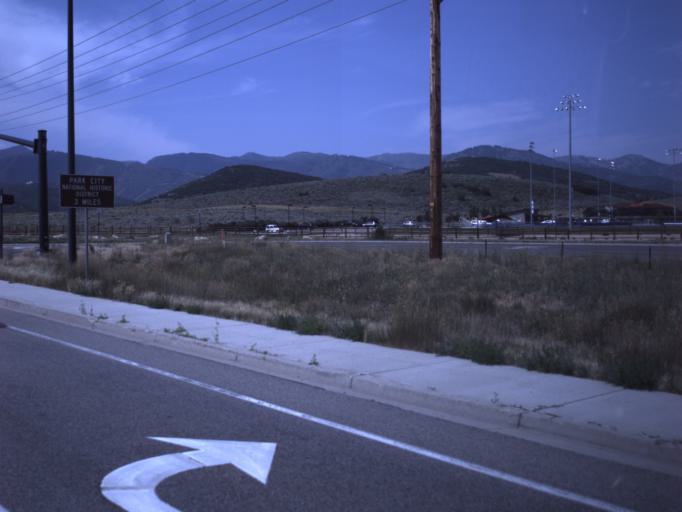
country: US
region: Utah
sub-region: Summit County
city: Park City
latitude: 40.6805
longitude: -111.4660
